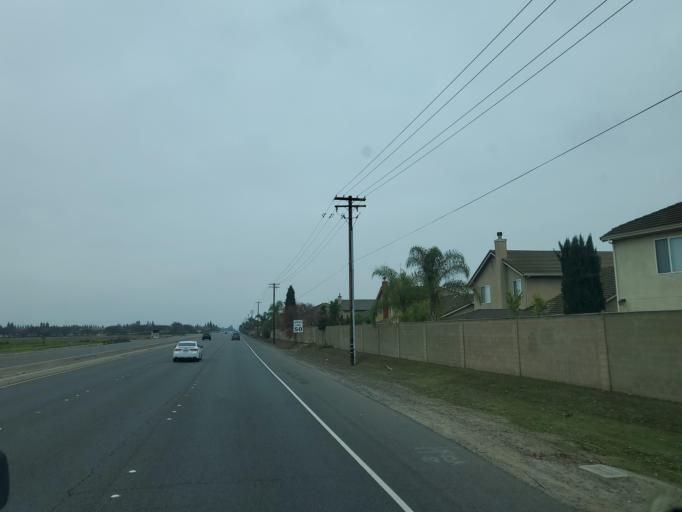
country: US
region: California
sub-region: Stanislaus County
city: Salida
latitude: 37.7002
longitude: -121.0475
